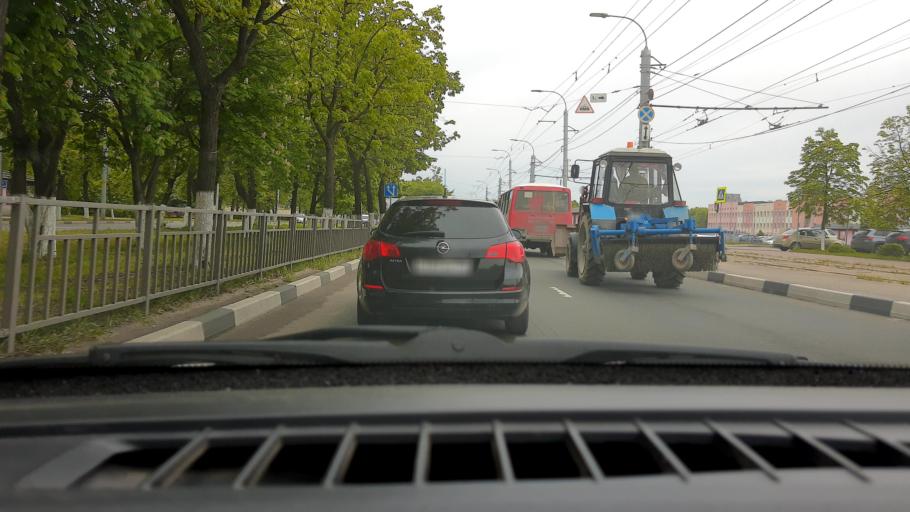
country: RU
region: Nizjnij Novgorod
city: Gorbatovka
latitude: 56.2471
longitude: 43.8811
